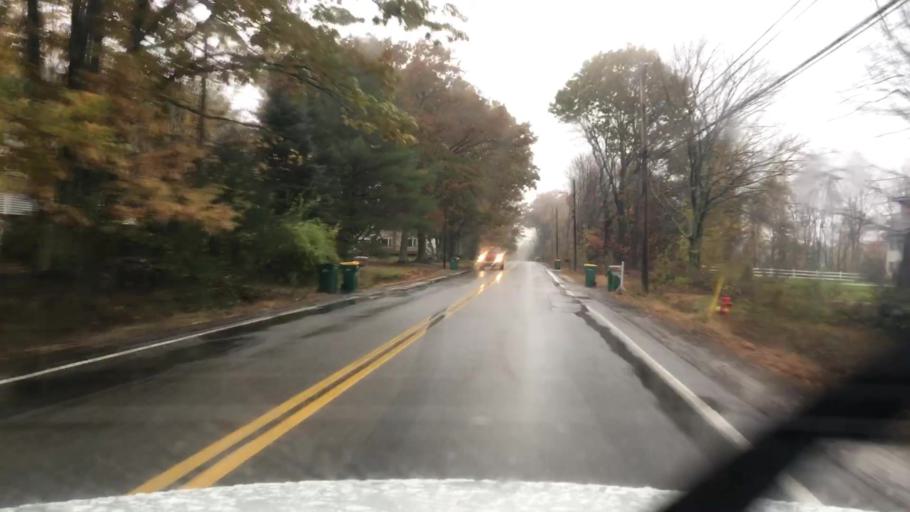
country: US
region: New Hampshire
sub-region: Strafford County
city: Rochester
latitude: 43.3153
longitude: -70.9358
